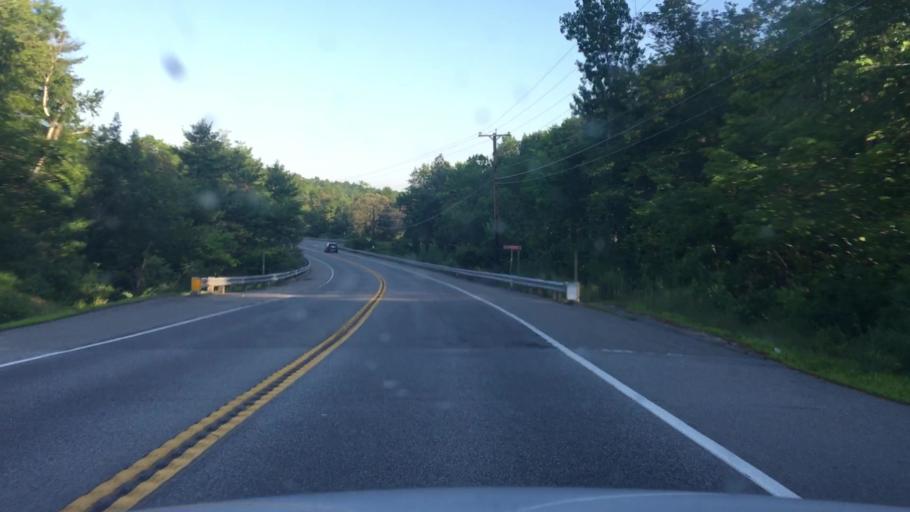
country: US
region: Maine
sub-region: Androscoggin County
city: Lisbon
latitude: 44.0138
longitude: -70.0896
